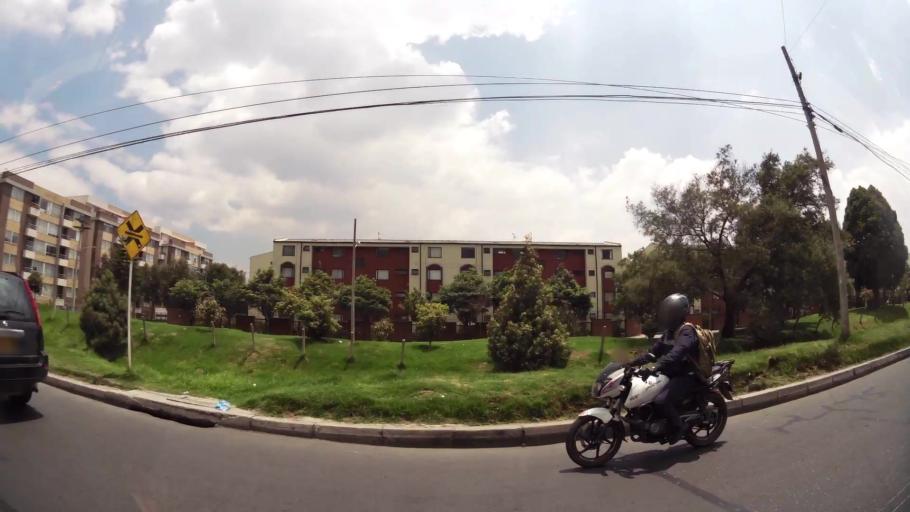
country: CO
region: Cundinamarca
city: La Calera
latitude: 4.7384
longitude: -74.0328
